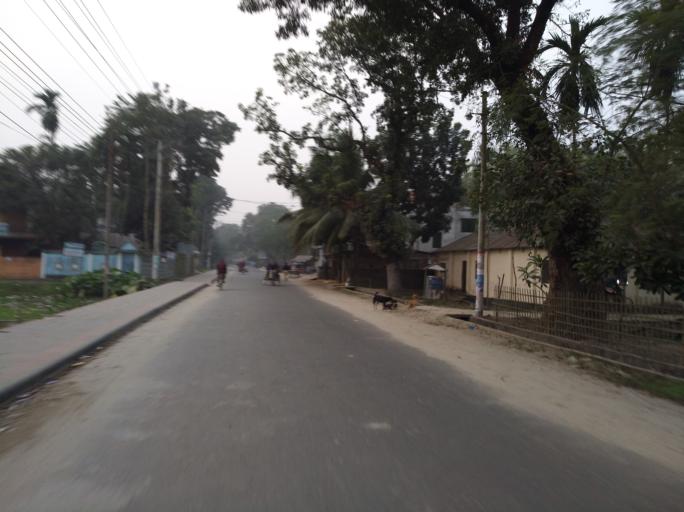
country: BD
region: Rajshahi
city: Saidpur
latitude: 25.9281
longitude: 88.8629
